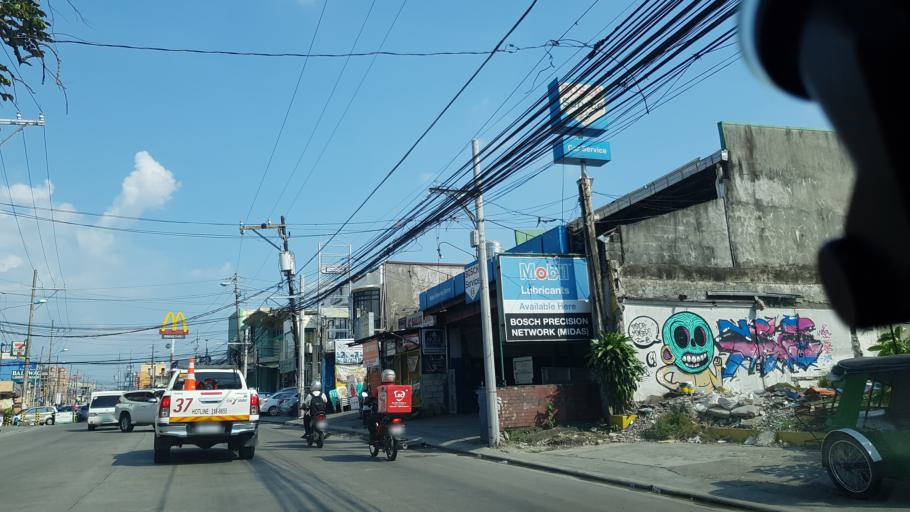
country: PH
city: Sambayanihan People's Village
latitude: 14.4852
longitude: 121.0292
